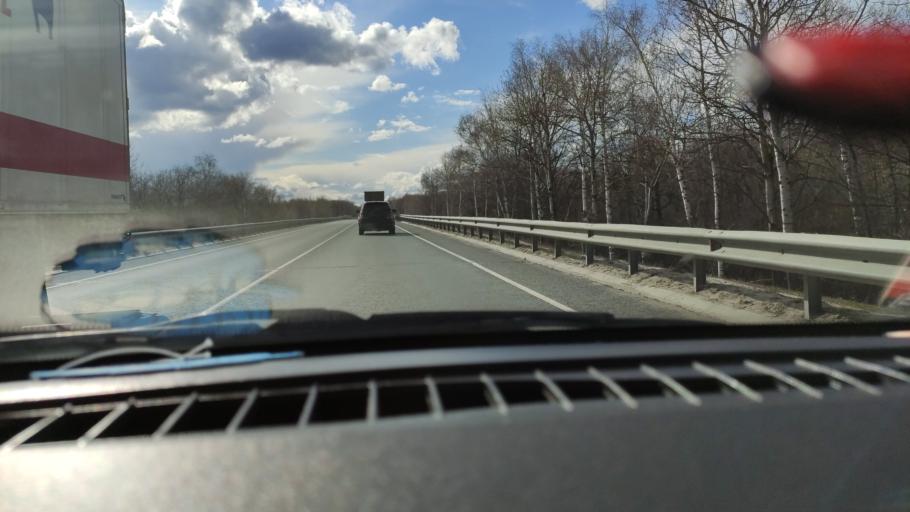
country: RU
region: Saratov
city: Vol'sk
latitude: 52.1092
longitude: 47.3764
